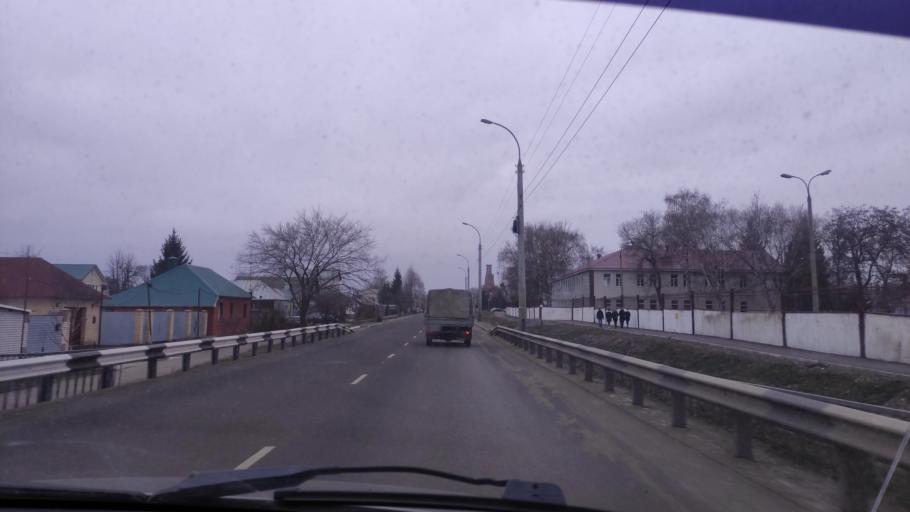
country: RU
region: Tambov
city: Tambov
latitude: 52.7217
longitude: 41.4195
